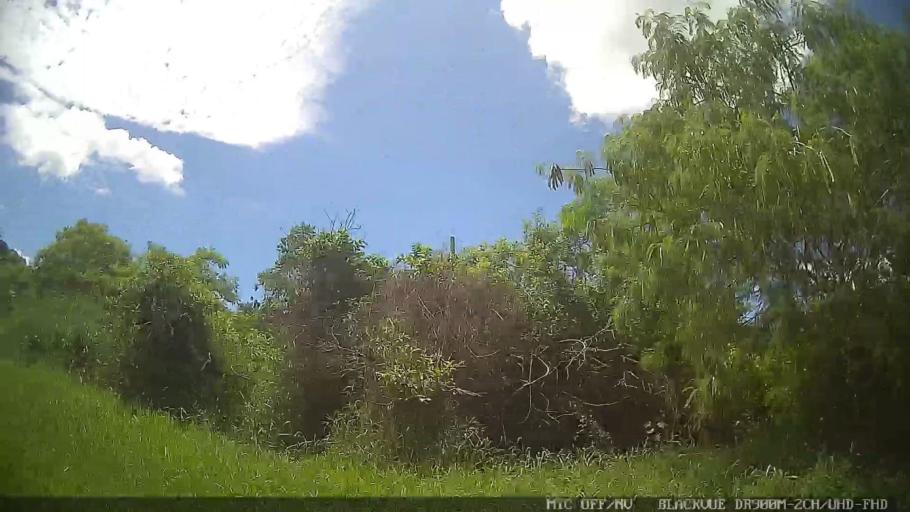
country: BR
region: Sao Paulo
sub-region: Biritiba-Mirim
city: Biritiba Mirim
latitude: -23.6022
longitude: -46.0621
